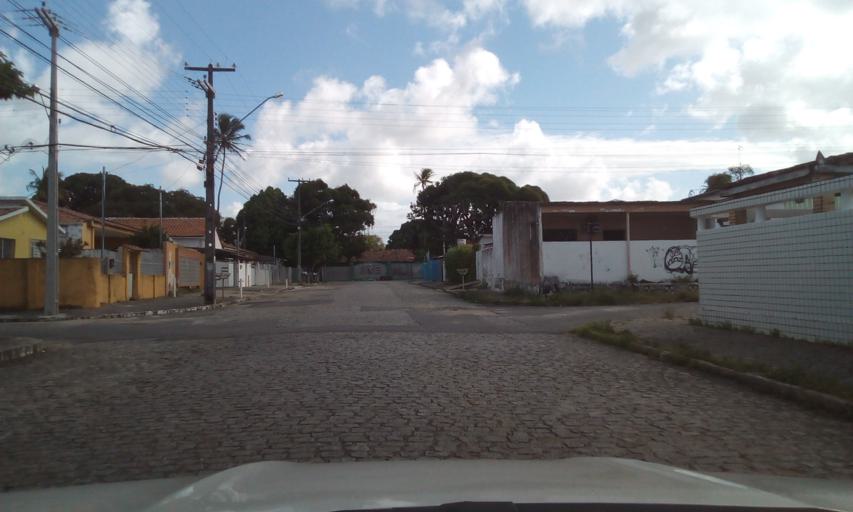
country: BR
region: Paraiba
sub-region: Joao Pessoa
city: Joao Pessoa
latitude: -7.1380
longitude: -34.8822
